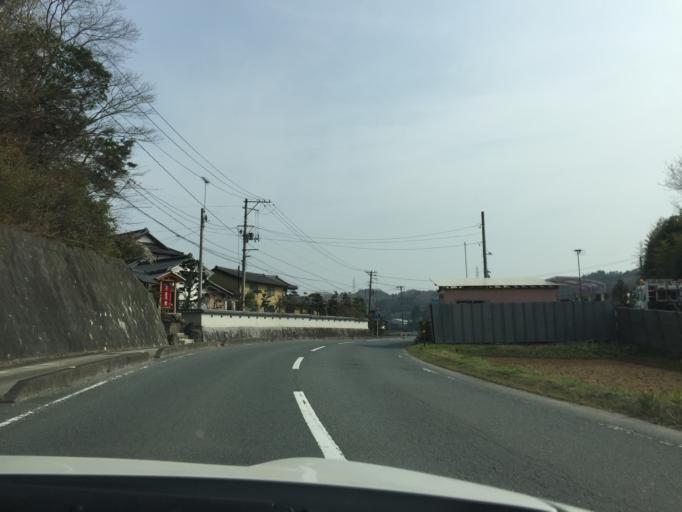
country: JP
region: Fukushima
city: Iwaki
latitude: 36.9658
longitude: 140.8105
